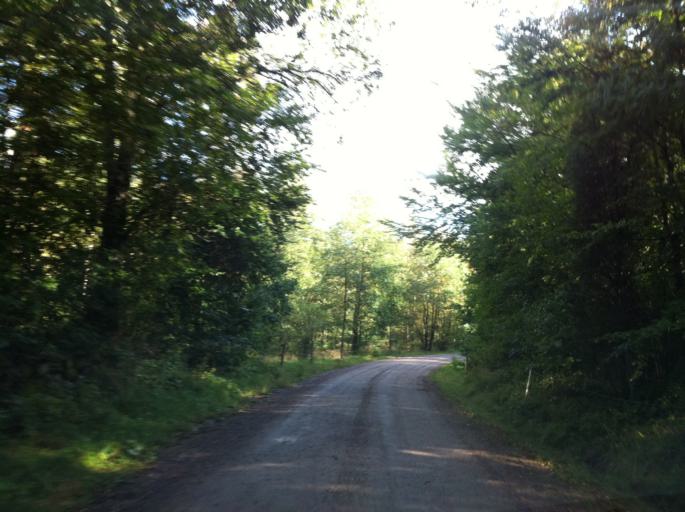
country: SE
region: Skane
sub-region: Hassleholms Kommun
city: Sosdala
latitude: 56.1274
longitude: 13.5918
